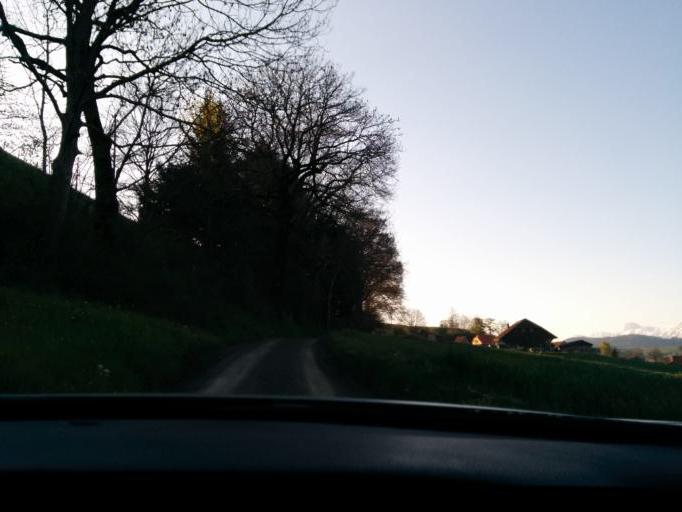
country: CH
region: Bern
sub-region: Bern-Mittelland District
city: Wahlern
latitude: 46.8388
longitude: 7.3964
